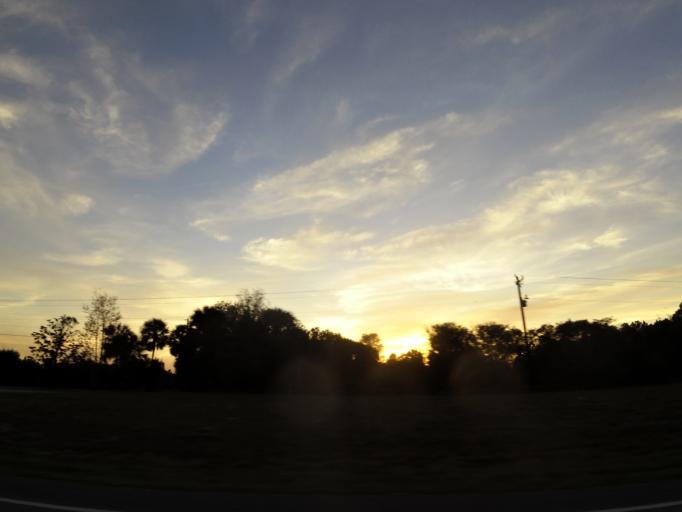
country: US
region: Florida
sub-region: Volusia County
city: De Leon Springs
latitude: 29.1628
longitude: -81.2972
